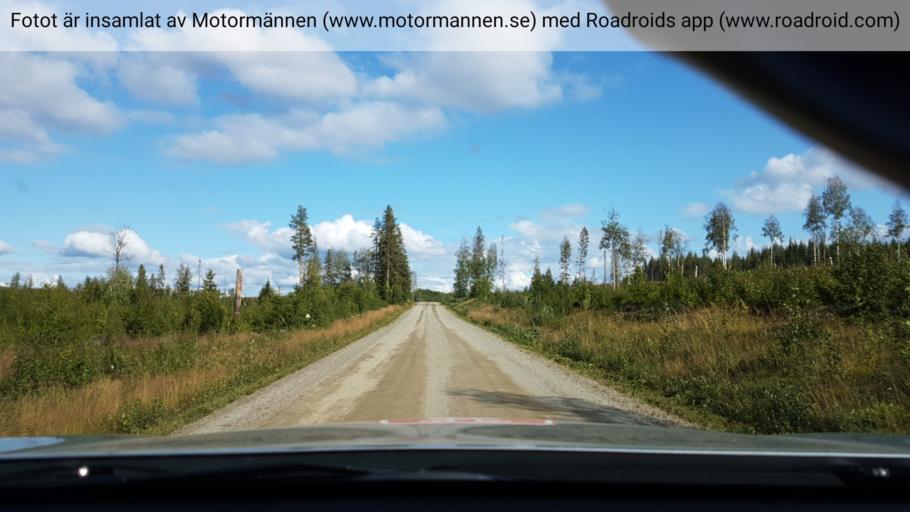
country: SE
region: Vaesterbotten
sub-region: Lycksele Kommun
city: Lycksele
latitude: 64.5792
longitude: 19.0582
